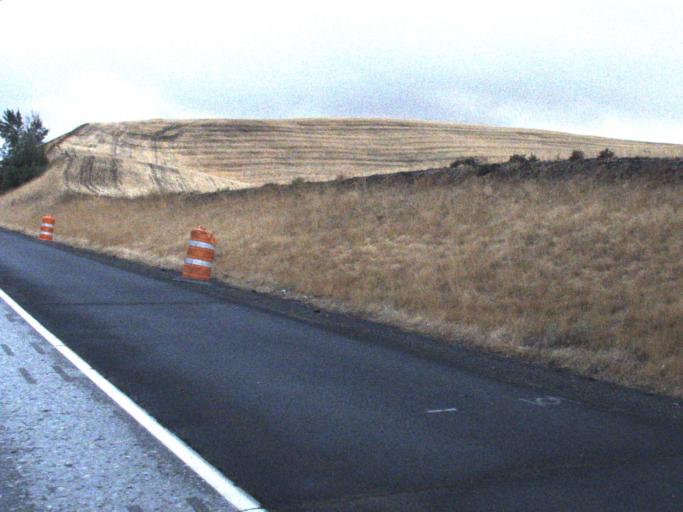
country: US
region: Washington
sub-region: Whitman County
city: Colfax
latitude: 47.0273
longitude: -117.3608
